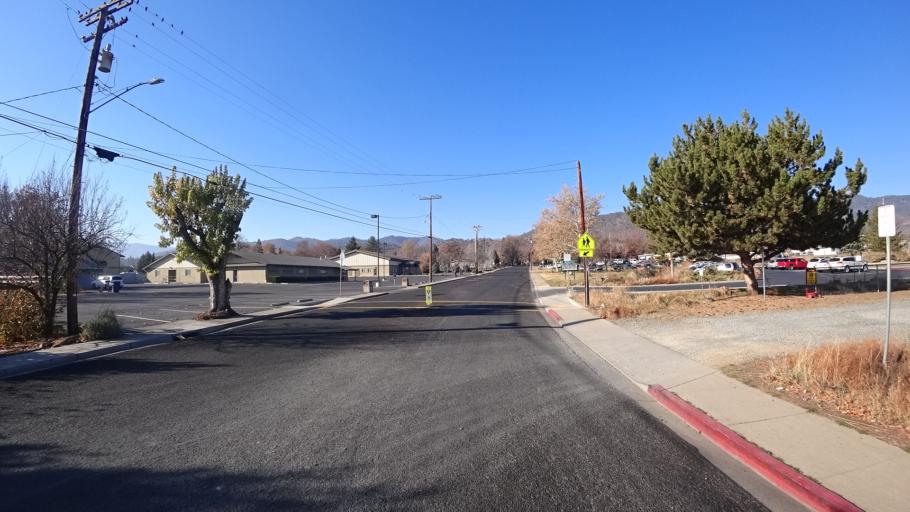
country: US
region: California
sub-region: Siskiyou County
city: Yreka
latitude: 41.7245
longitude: -122.6429
